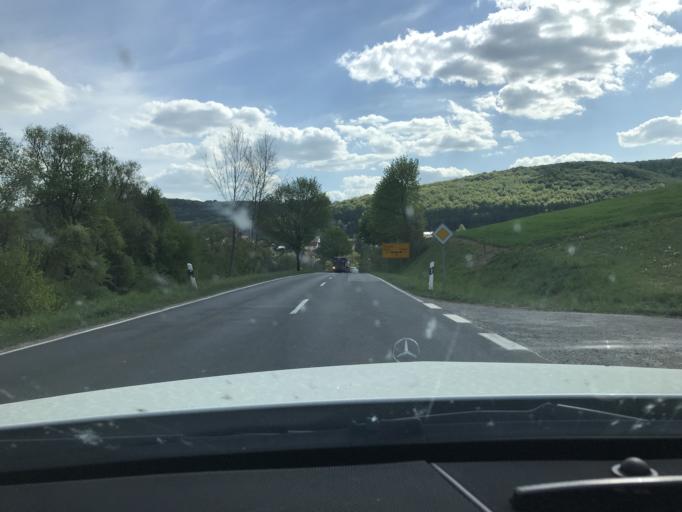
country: DE
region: Hesse
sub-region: Regierungsbezirk Kassel
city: Weissenborn
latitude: 51.1093
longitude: 10.0551
